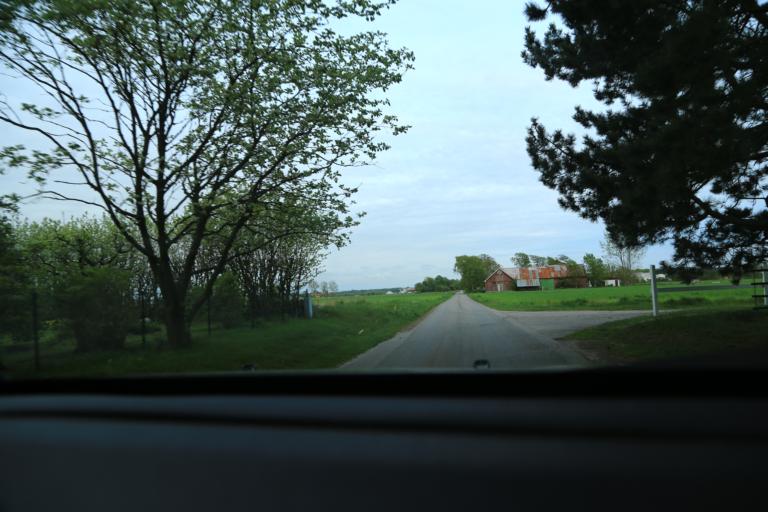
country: SE
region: Halland
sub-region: Varbergs Kommun
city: Varberg
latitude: 57.1516
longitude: 12.2379
